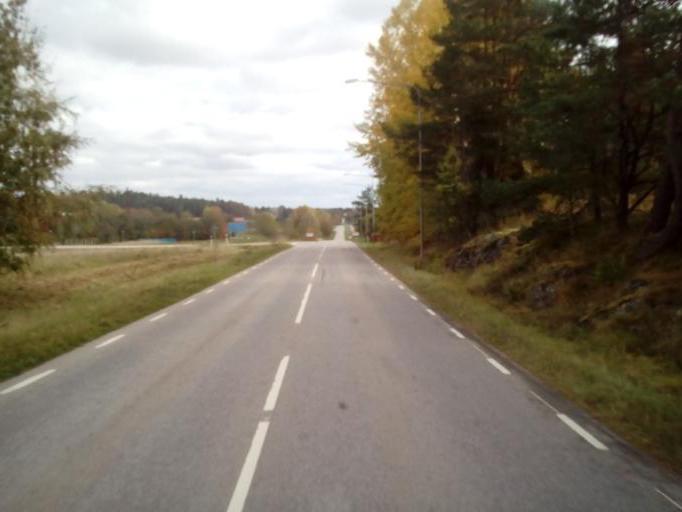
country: SE
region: Kalmar
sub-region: Vasterviks Kommun
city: Gamleby
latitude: 57.8900
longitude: 16.3872
